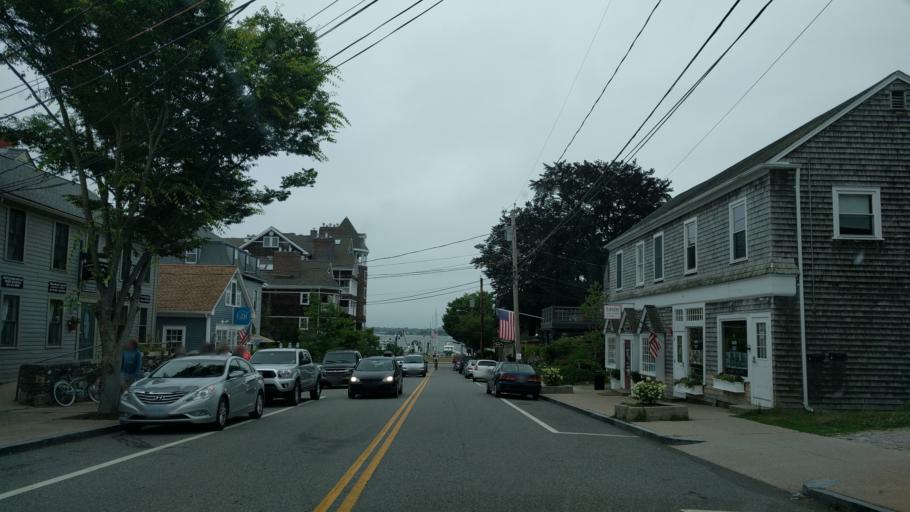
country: US
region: Rhode Island
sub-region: Newport County
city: Jamestown
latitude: 41.4963
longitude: -71.3688
